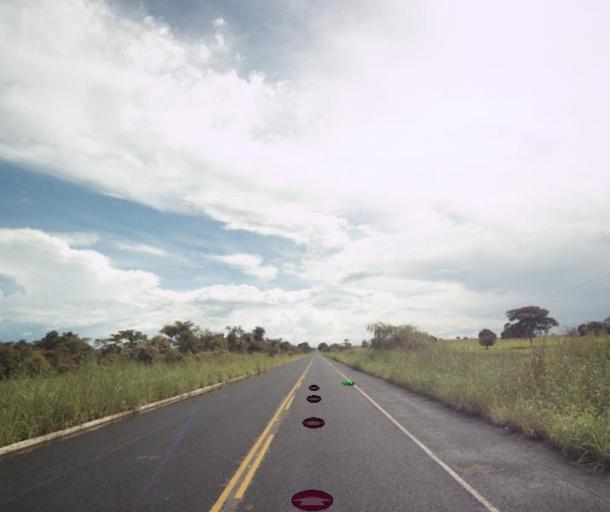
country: BR
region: Goias
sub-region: Sao Miguel Do Araguaia
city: Sao Miguel do Araguaia
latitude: -13.2944
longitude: -50.2298
